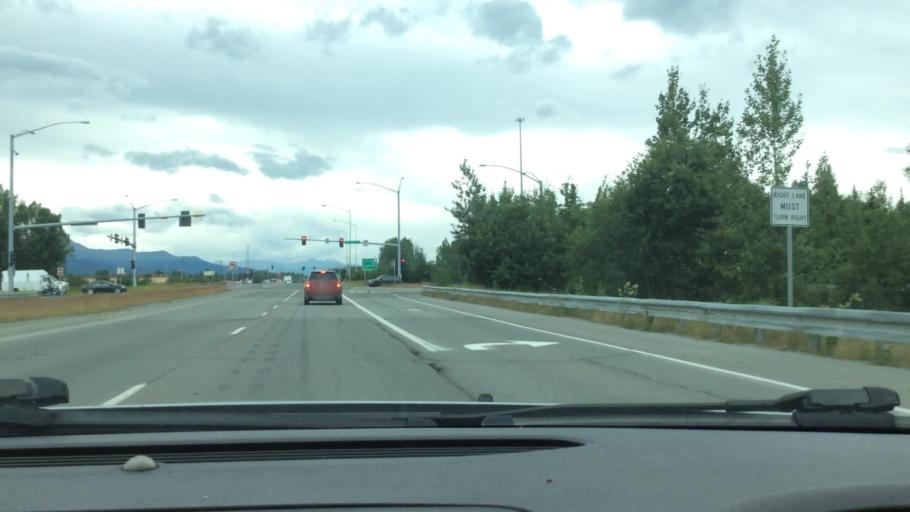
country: US
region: Alaska
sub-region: Anchorage Municipality
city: Anchorage
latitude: 61.2272
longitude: -149.7786
